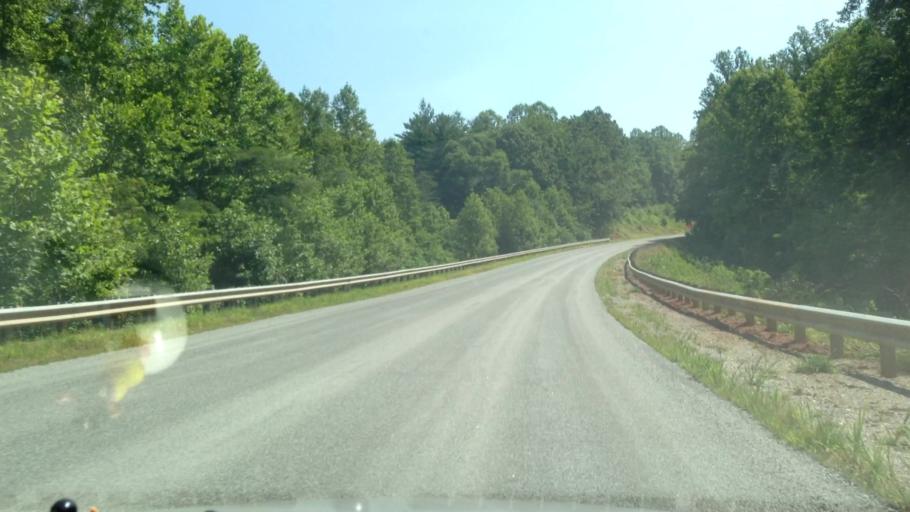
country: US
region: Virginia
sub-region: Patrick County
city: Stuart
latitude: 36.5978
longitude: -80.3066
